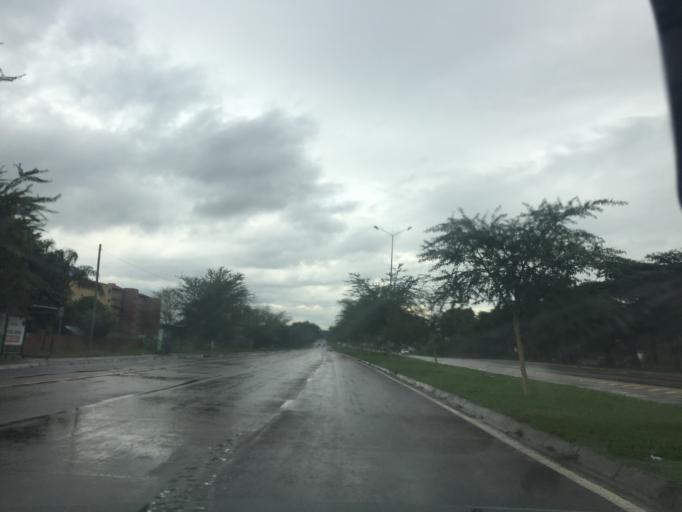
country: ZA
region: Gauteng
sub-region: City of Tshwane Metropolitan Municipality
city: Pretoria
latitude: -25.7669
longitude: 28.3026
